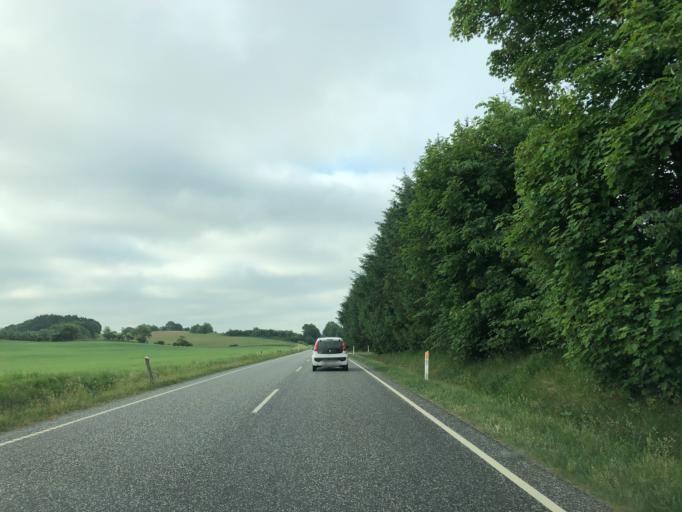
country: DK
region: South Denmark
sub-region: Vejle Kommune
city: Give
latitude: 55.7803
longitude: 9.2786
